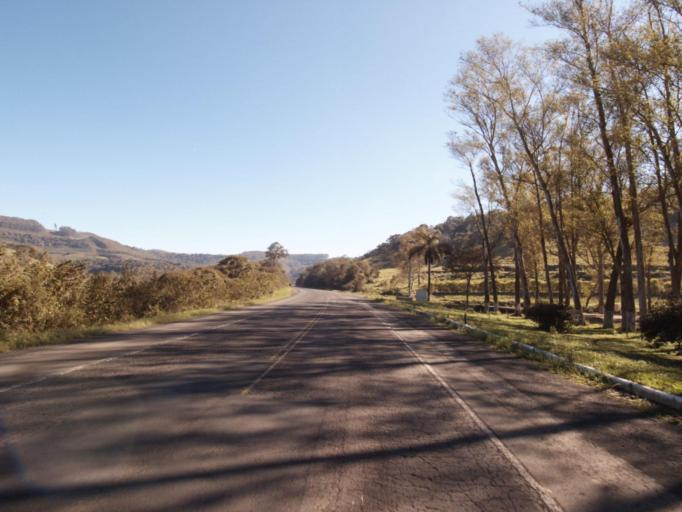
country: BR
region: Rio Grande do Sul
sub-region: Frederico Westphalen
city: Frederico Westphalen
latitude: -27.0369
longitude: -53.2301
